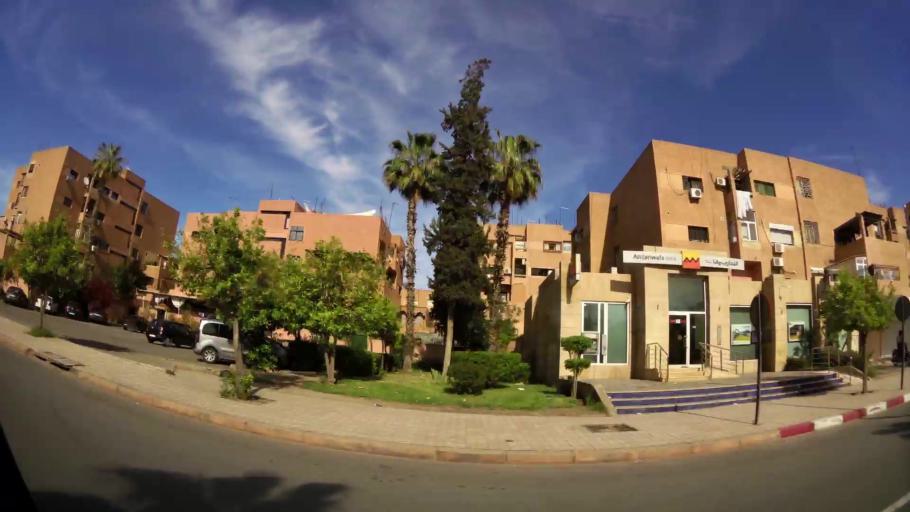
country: MA
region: Marrakech-Tensift-Al Haouz
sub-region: Marrakech
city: Marrakesh
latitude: 31.6458
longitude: -8.0006
